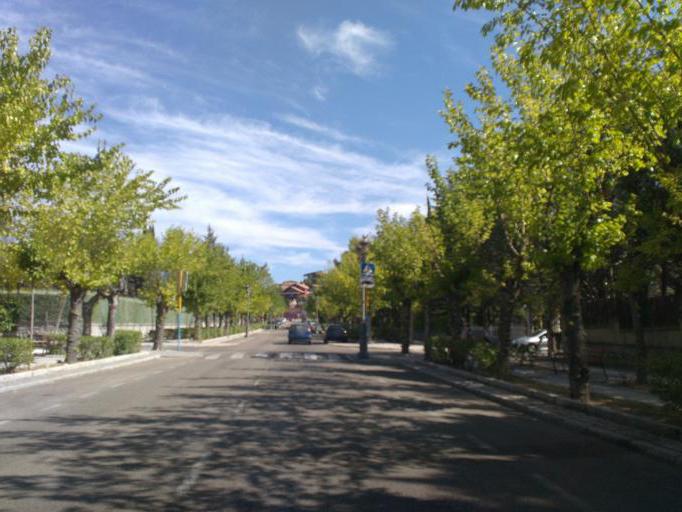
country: ES
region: Madrid
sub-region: Provincia de Madrid
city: Torrelodones
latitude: 40.5828
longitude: -3.9539
